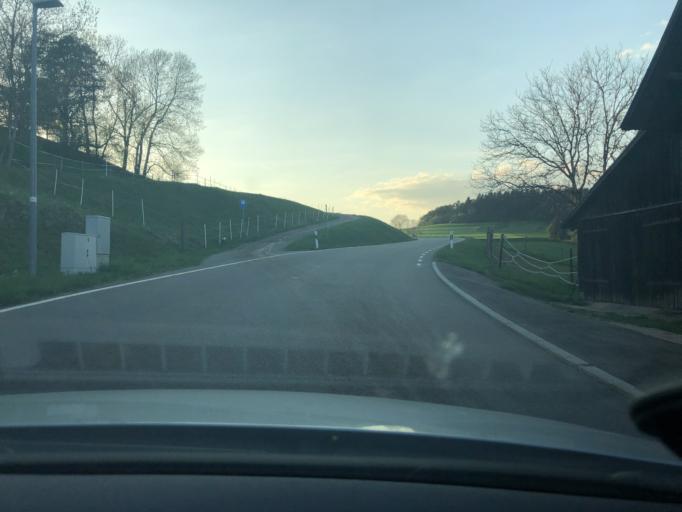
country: DE
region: Baden-Wuerttemberg
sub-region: Freiburg Region
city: Dogern
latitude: 47.6599
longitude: 8.1689
